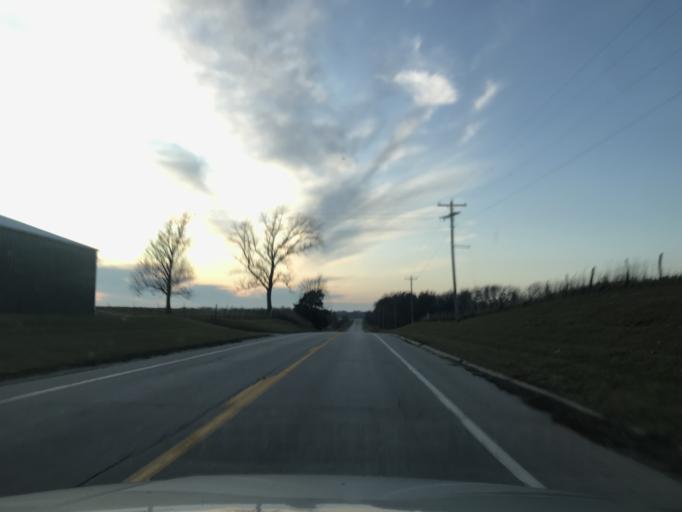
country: US
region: Illinois
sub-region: Henderson County
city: Oquawka
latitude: 41.0186
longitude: -90.8018
